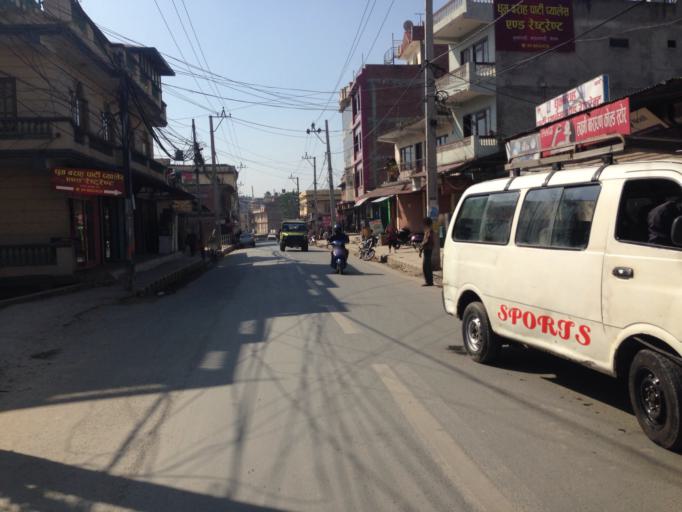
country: NP
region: Central Region
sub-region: Bagmati Zone
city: Kathmandu
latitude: 27.7234
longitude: 85.3391
